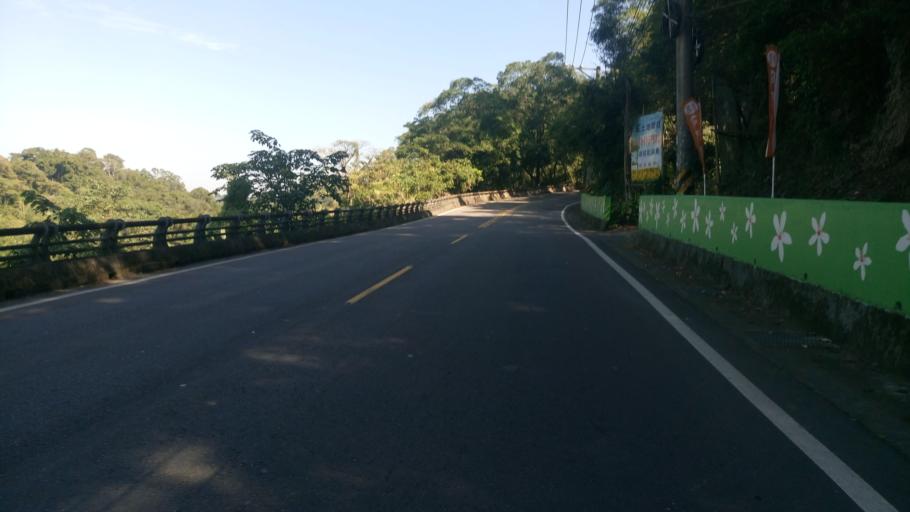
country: TW
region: Taiwan
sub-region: Hsinchu
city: Zhubei
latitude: 24.7185
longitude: 121.1582
